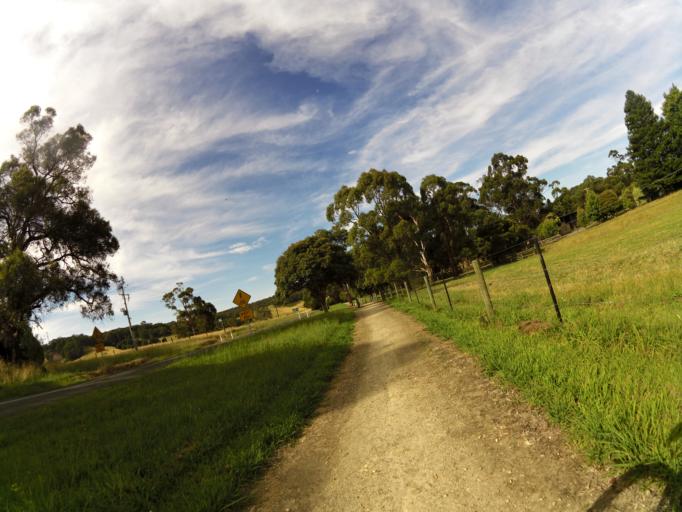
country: AU
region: Victoria
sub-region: Colac-Otway
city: Colac
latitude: -38.5123
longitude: 143.7162
